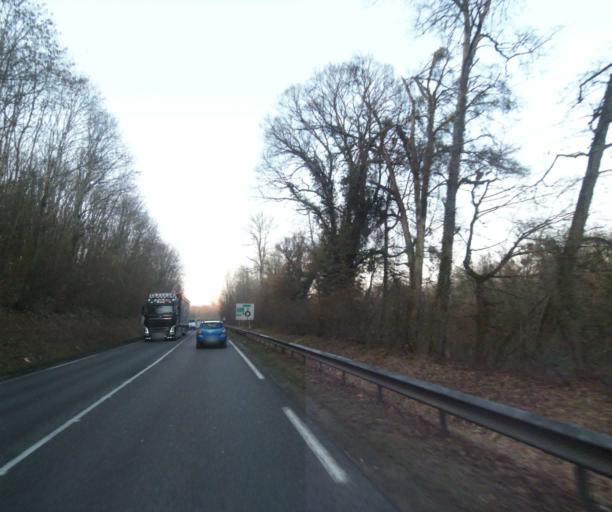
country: FR
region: Lorraine
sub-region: Departement de la Meuse
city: Ancerville
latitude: 48.6208
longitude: 4.9947
